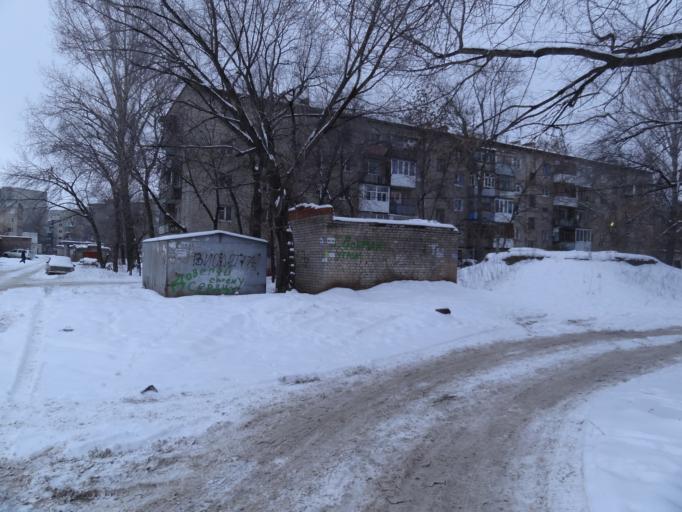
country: RU
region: Saratov
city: Engel's
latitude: 51.4821
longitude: 46.1457
